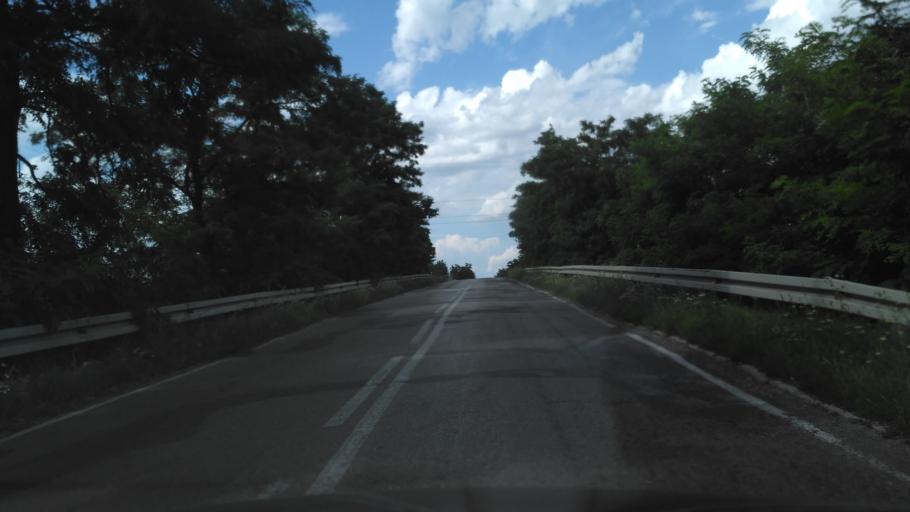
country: PL
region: Lublin Voivodeship
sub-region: Powiat leczynski
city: Milejow
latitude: 51.1943
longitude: 22.9390
